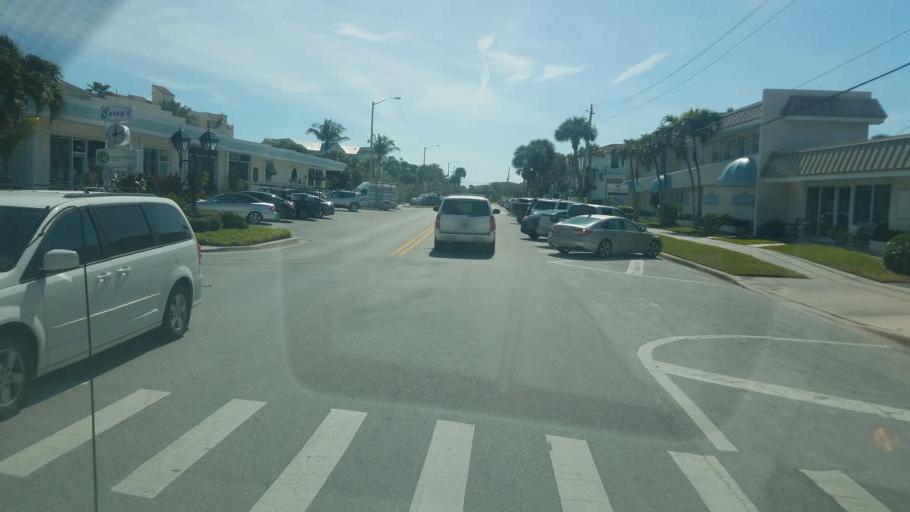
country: US
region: Florida
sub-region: Indian River County
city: Vero Beach
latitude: 27.6495
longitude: -80.3555
